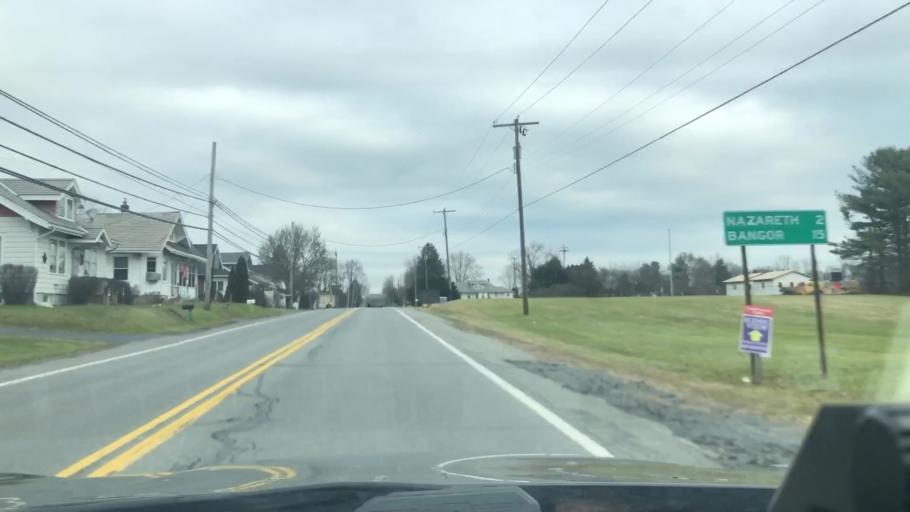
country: US
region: Pennsylvania
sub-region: Northampton County
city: Nazareth
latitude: 40.7076
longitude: -75.3274
